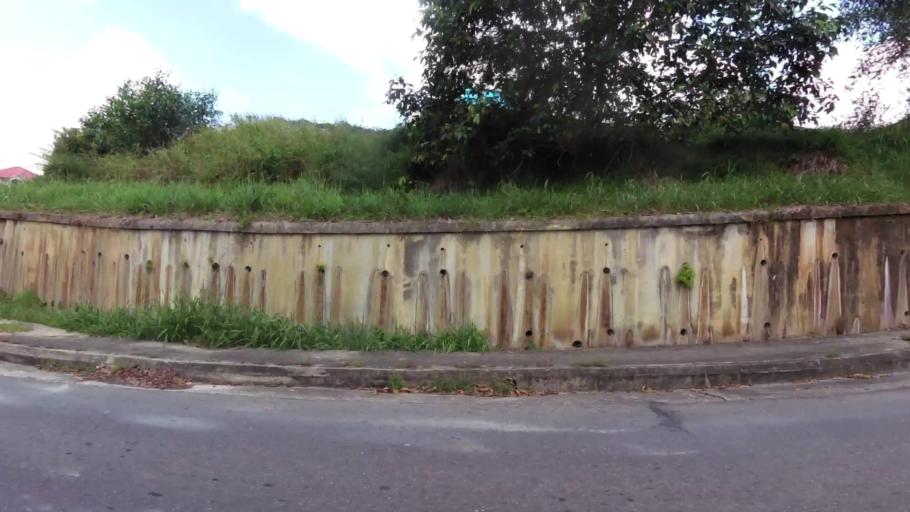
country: BN
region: Brunei and Muara
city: Bandar Seri Begawan
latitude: 4.9430
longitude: 114.9661
